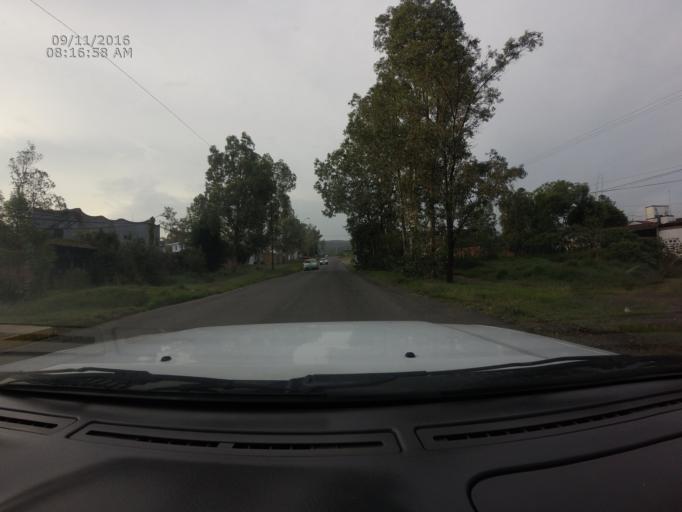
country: MX
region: Michoacan
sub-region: Morelia
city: Morelos
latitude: 19.6479
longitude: -101.2305
